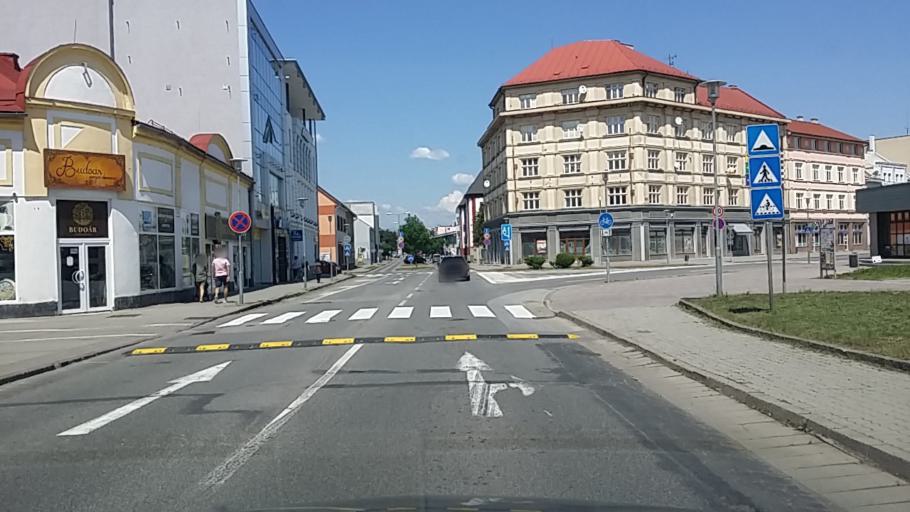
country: SK
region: Banskobystricky
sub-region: Okres Banska Bystrica
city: Zvolen
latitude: 48.5753
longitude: 19.1291
